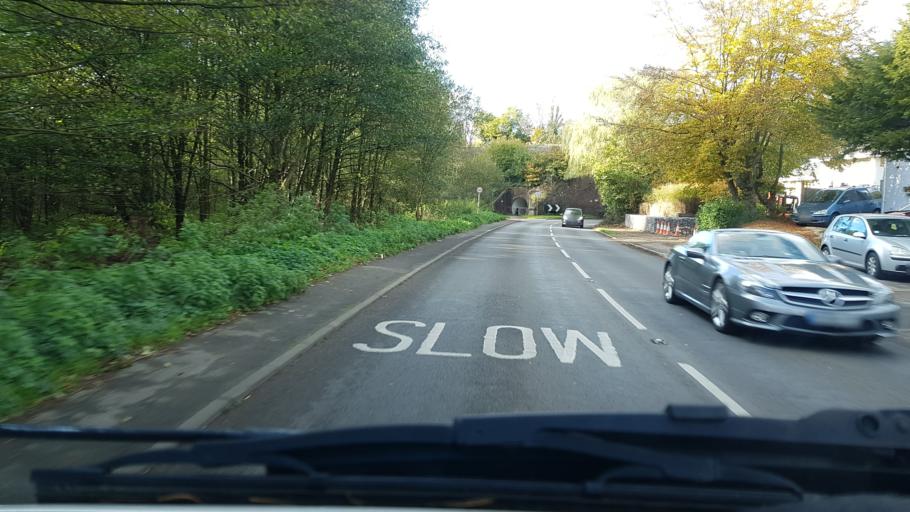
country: GB
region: England
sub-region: Surrey
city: East Horsley
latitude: 51.2182
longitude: -0.4425
